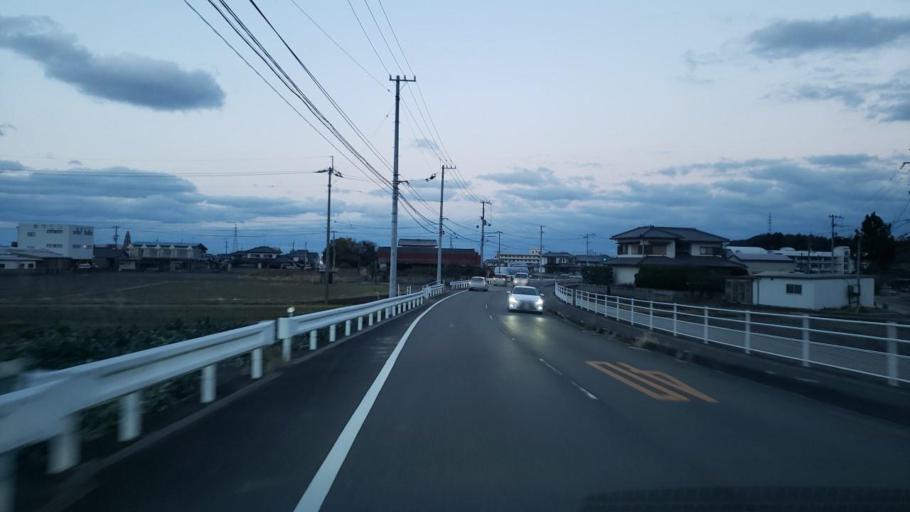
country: JP
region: Tokushima
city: Kamojimacho-jogejima
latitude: 34.2354
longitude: 134.3477
